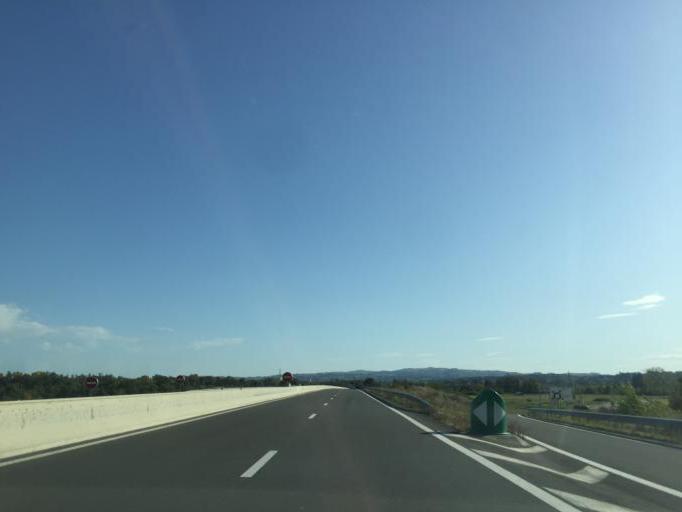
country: FR
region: Rhone-Alpes
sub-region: Departement de la Loire
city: Bonson
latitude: 45.5143
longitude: 4.2267
